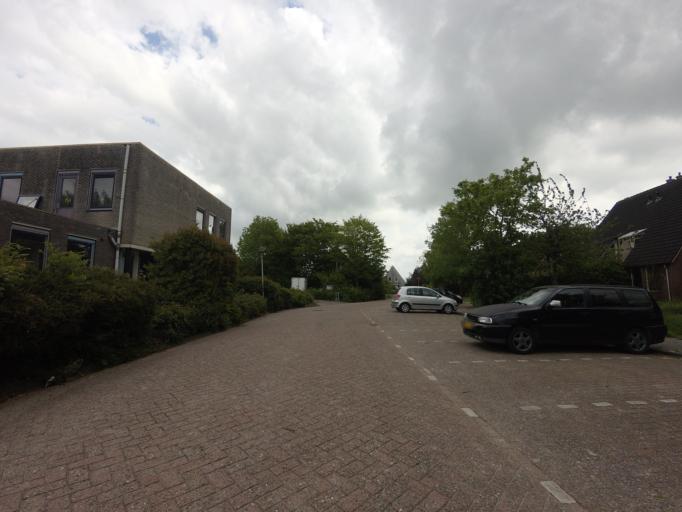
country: NL
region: Friesland
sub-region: Gemeente Littenseradiel
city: Wommels
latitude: 53.1075
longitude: 5.5926
